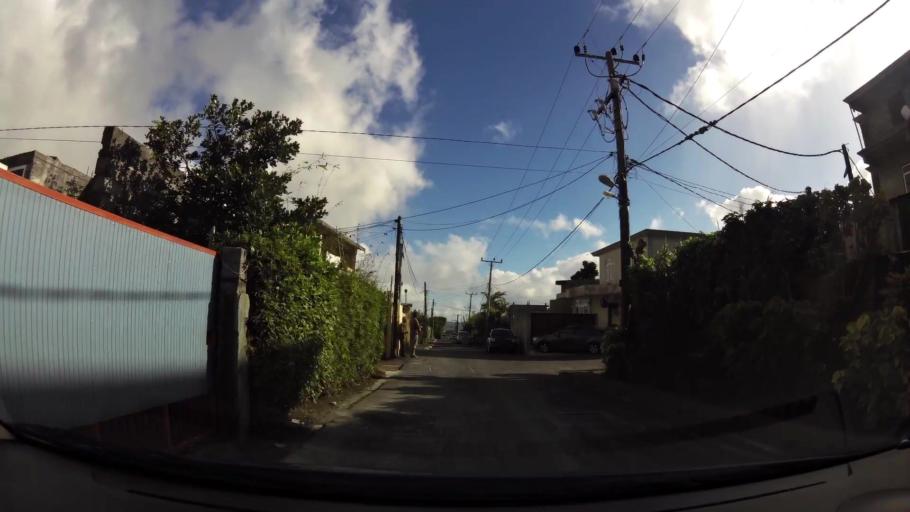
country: MU
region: Plaines Wilhems
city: Curepipe
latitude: -20.3240
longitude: 57.5089
